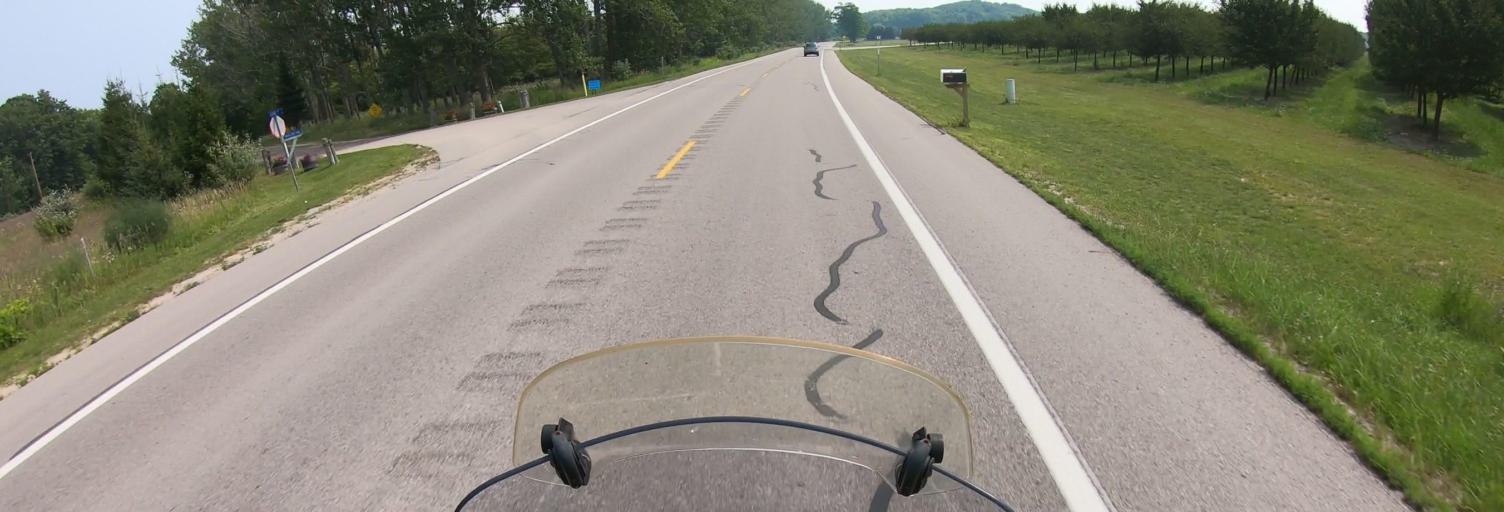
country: US
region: Michigan
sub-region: Leelanau County
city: Leland
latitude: 45.0916
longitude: -85.6042
